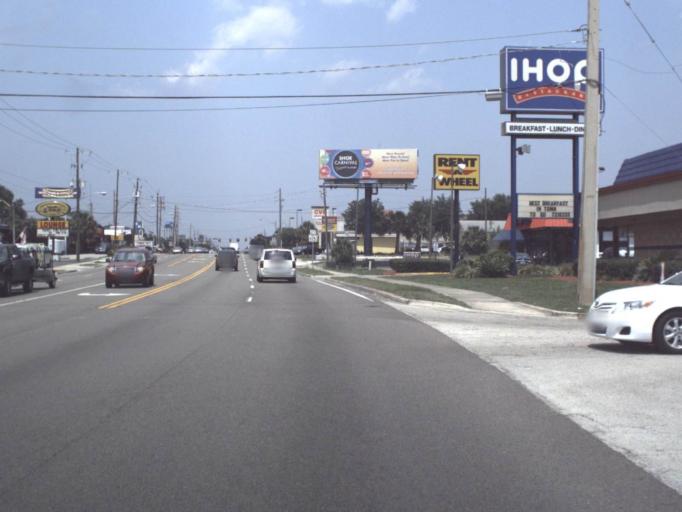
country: US
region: Florida
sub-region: Duval County
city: Jacksonville
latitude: 30.3146
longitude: -81.5621
